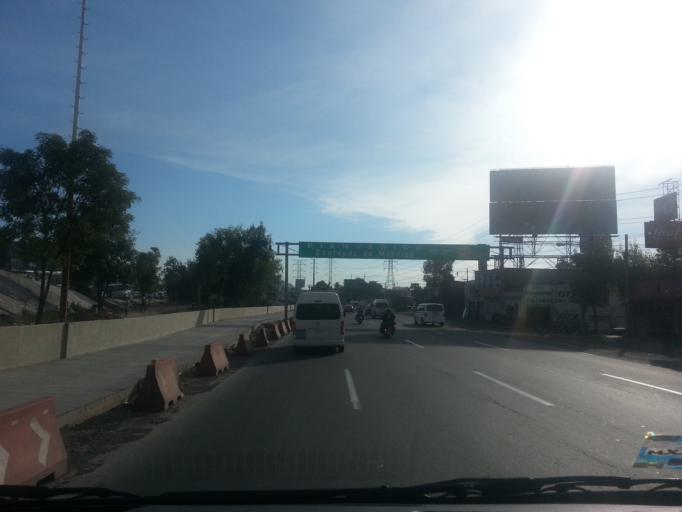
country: MX
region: Mexico
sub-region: Tlalnepantla de Baz
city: Puerto Escondido (Tepeolulco Puerto Escondido)
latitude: 19.5218
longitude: -99.0910
